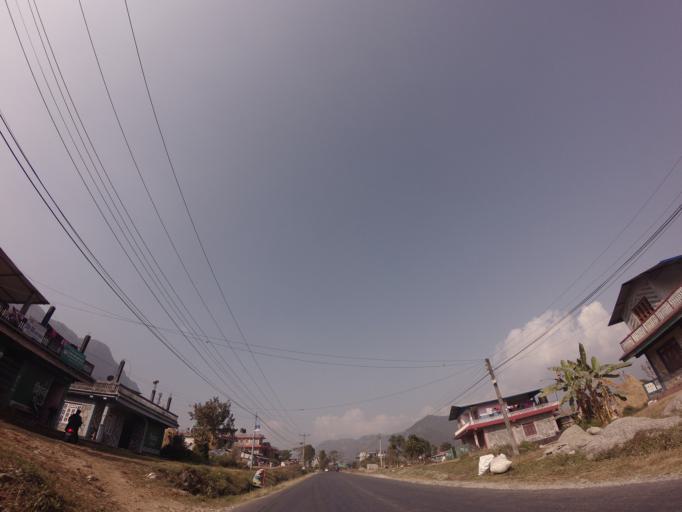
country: NP
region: Western Region
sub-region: Gandaki Zone
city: Pokhara
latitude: 28.2738
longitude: 83.9418
